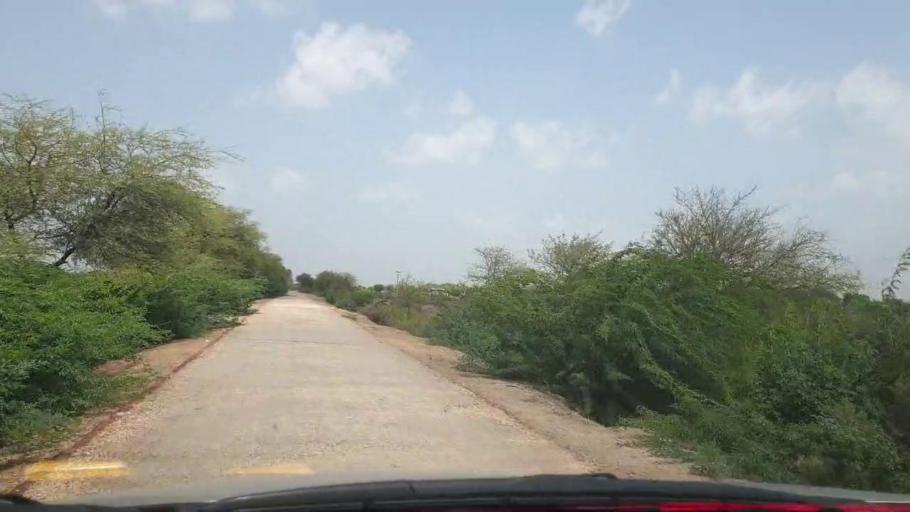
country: PK
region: Sindh
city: Rajo Khanani
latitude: 24.9162
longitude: 68.8980
